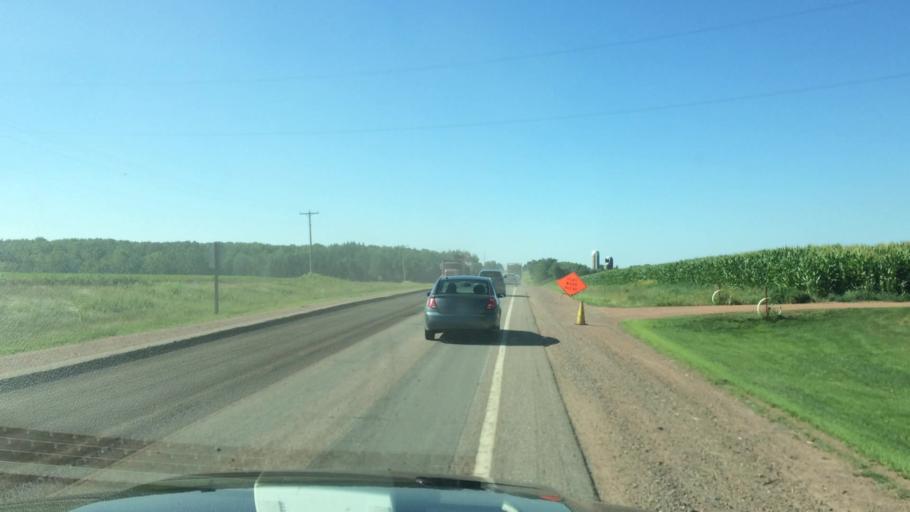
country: US
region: Wisconsin
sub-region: Marathon County
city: Stratford
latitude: 44.9002
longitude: -90.0787
